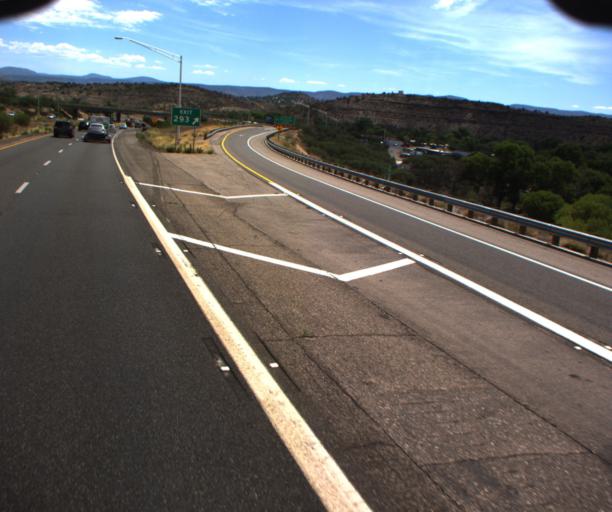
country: US
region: Arizona
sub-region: Yavapai County
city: Lake Montezuma
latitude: 34.6379
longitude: -111.8201
